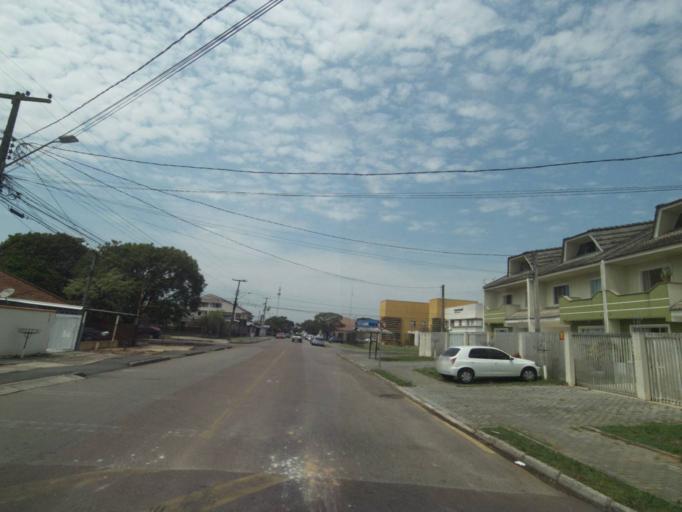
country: BR
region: Parana
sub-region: Pinhais
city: Pinhais
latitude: -25.4196
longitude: -49.2004
